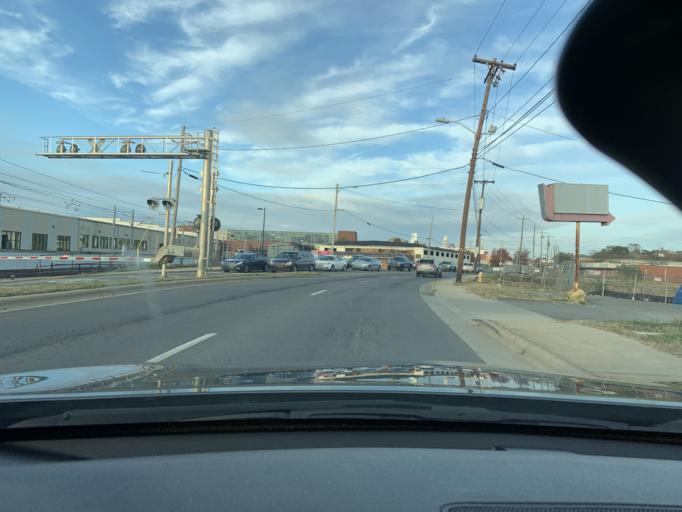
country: US
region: North Carolina
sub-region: Mecklenburg County
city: Charlotte
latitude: 35.1951
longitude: -80.8724
